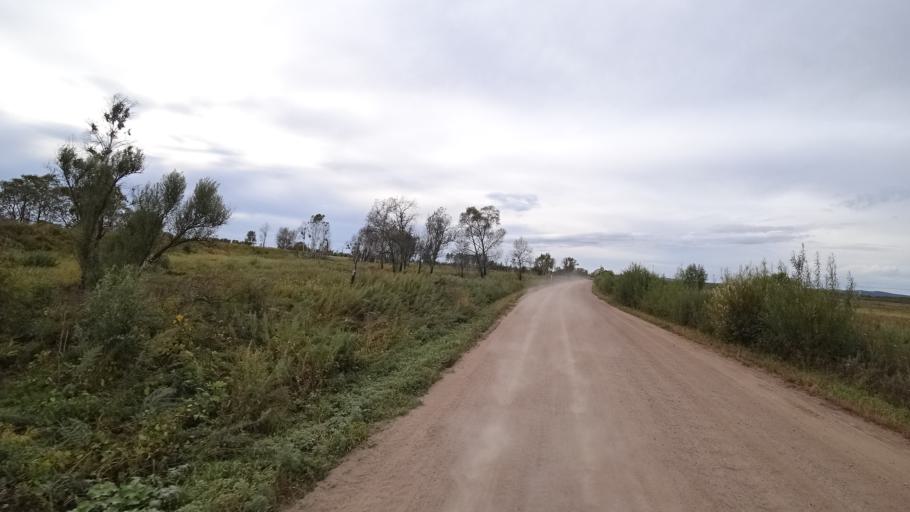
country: RU
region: Amur
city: Arkhara
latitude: 49.3767
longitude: 130.1815
